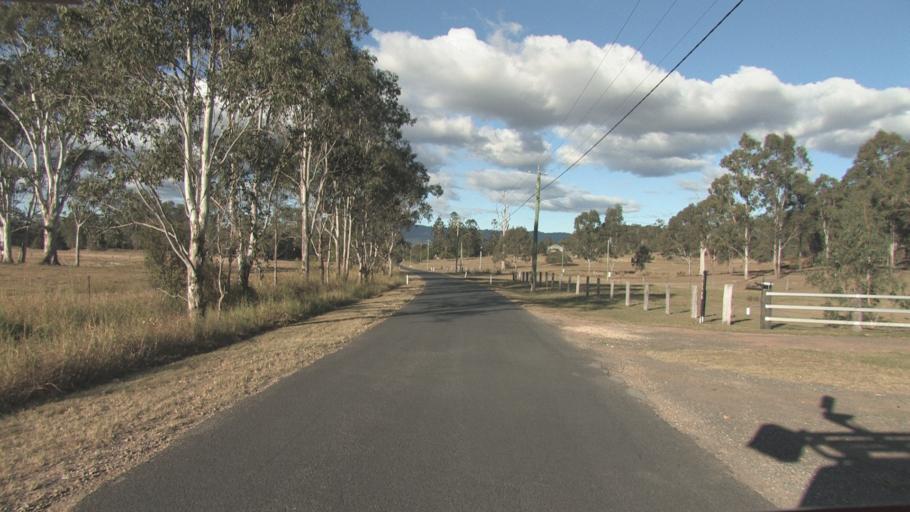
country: AU
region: Queensland
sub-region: Logan
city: Cedar Vale
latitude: -27.9286
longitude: 153.0742
